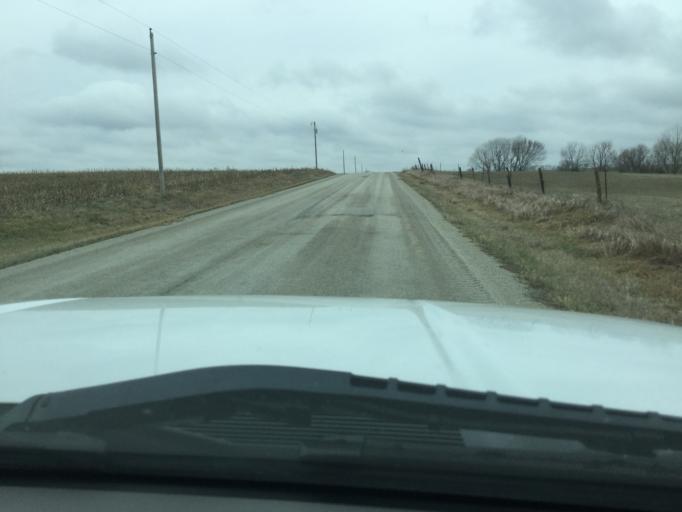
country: US
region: Kansas
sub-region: Nemaha County
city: Sabetha
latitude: 39.7980
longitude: -95.7535
